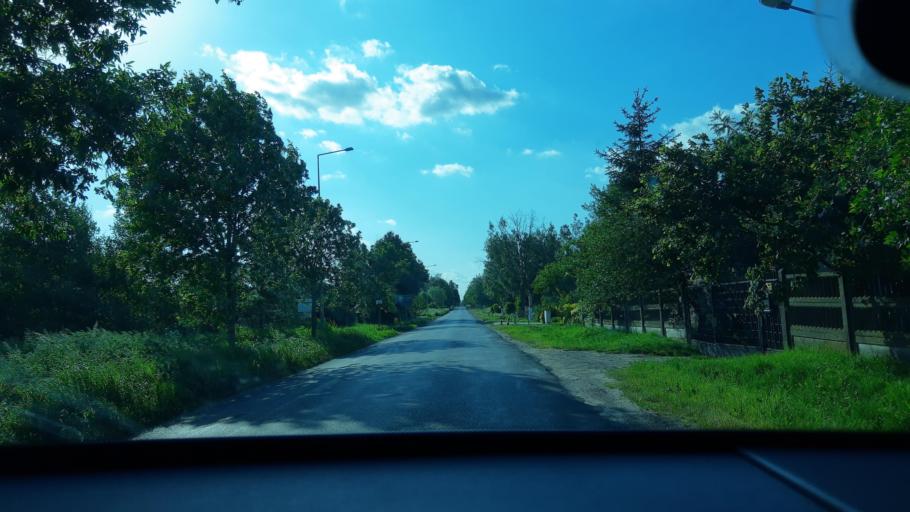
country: PL
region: Lodz Voivodeship
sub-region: Powiat sieradzki
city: Sieradz
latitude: 51.5491
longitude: 18.7744
